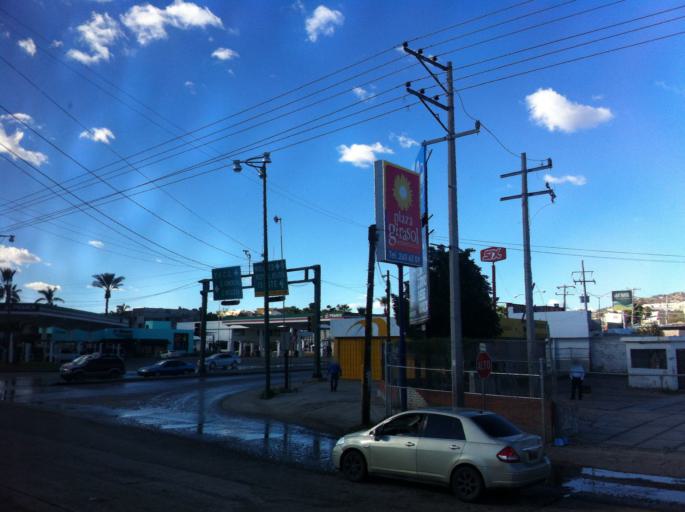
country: MX
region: Sonora
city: Hermosillo
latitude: 29.0978
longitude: -110.9254
